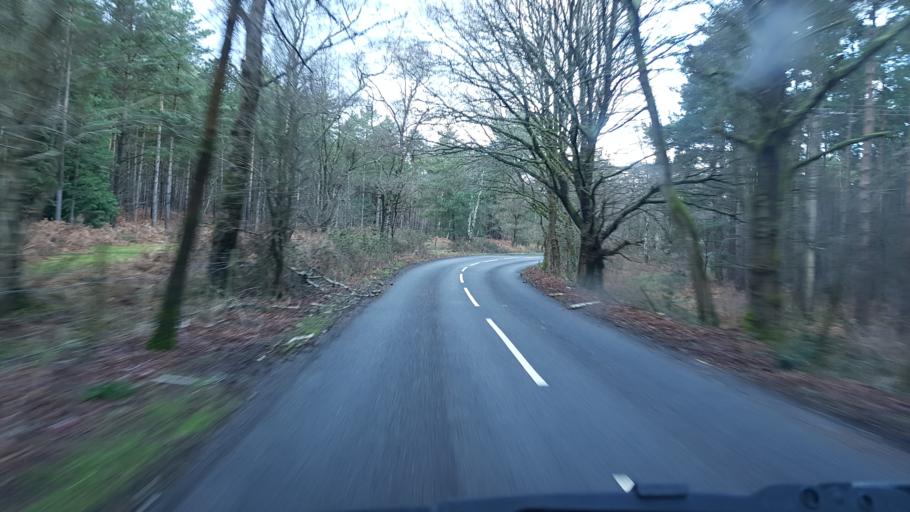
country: GB
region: England
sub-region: Surrey
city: Elstead
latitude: 51.1984
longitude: -0.7179
